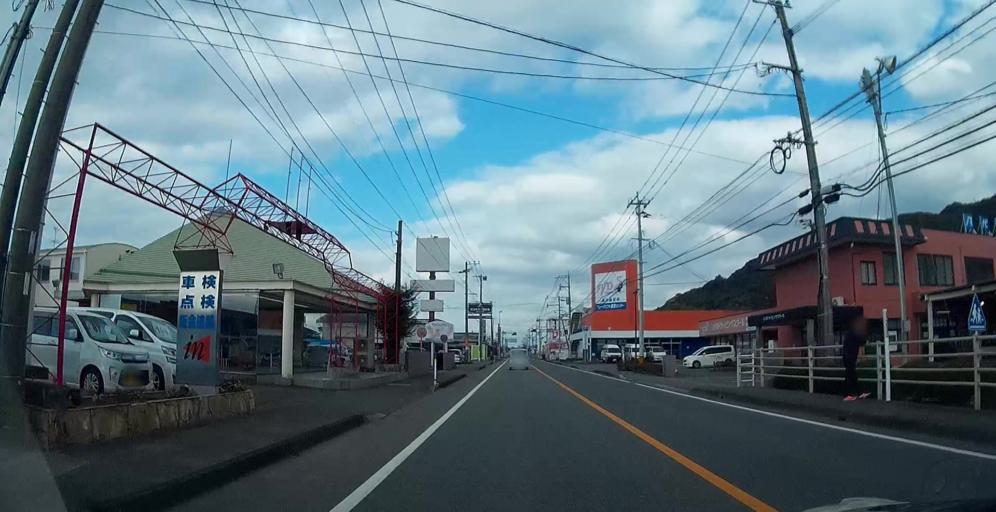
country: JP
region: Kumamoto
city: Yatsushiro
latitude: 32.4692
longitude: 130.6066
